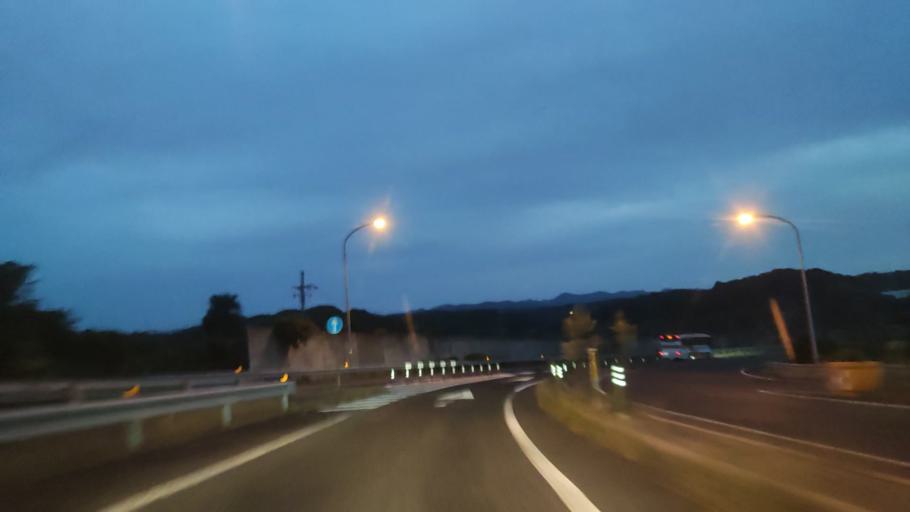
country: JP
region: Hyogo
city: Sandacho
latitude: 34.8888
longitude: 135.1175
